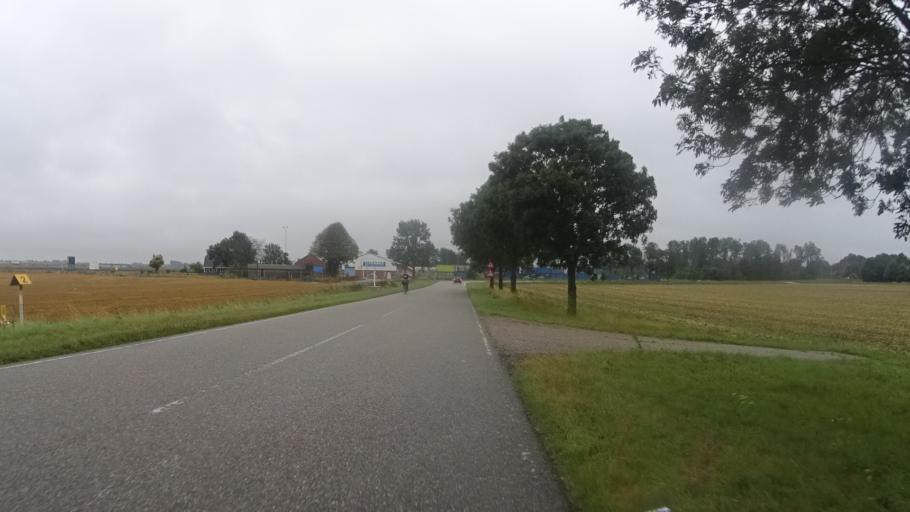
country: NL
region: Groningen
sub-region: Gemeente  Oldambt
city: Winschoten
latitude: 53.1858
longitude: 6.9488
